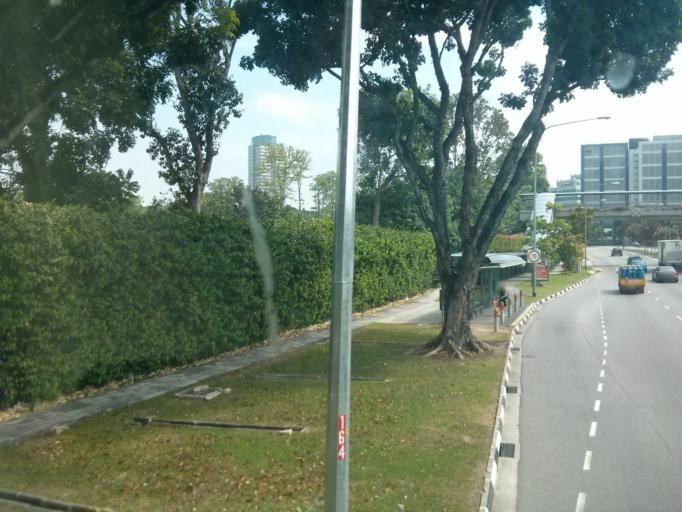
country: SG
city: Singapore
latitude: 1.3249
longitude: 103.7456
